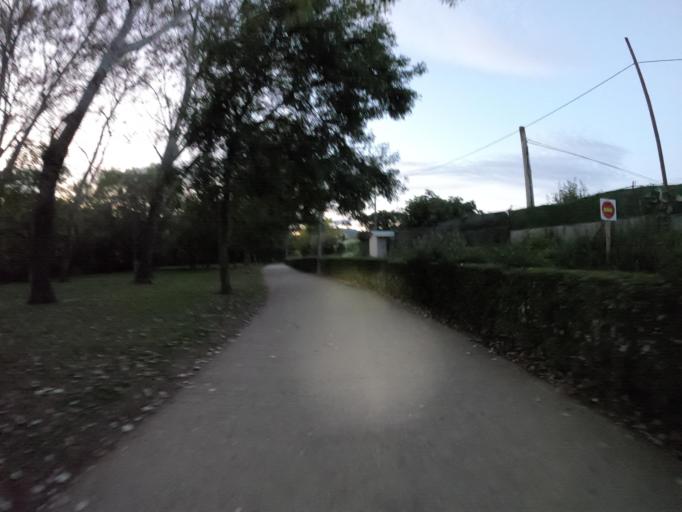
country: ES
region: Navarre
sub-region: Provincia de Navarra
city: Pamplona
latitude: 42.8188
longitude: -1.6356
